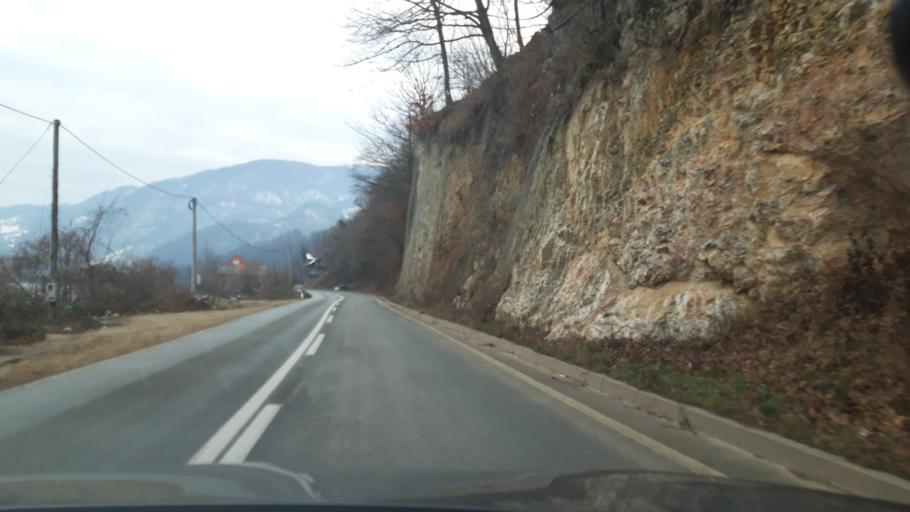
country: RS
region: Central Serbia
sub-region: Macvanski Okrug
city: Mali Zvornik
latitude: 44.3310
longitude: 19.1286
